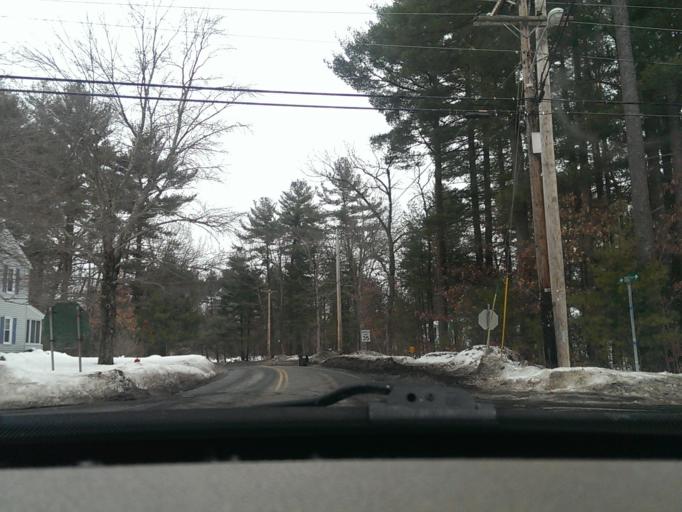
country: US
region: Massachusetts
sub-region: Hampden County
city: Wilbraham
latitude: 42.0925
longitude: -72.4620
